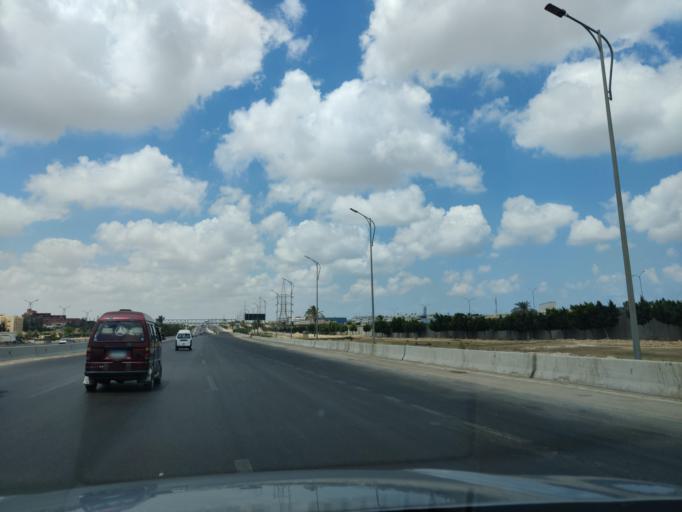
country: EG
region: Alexandria
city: Alexandria
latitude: 31.0277
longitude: 29.7785
